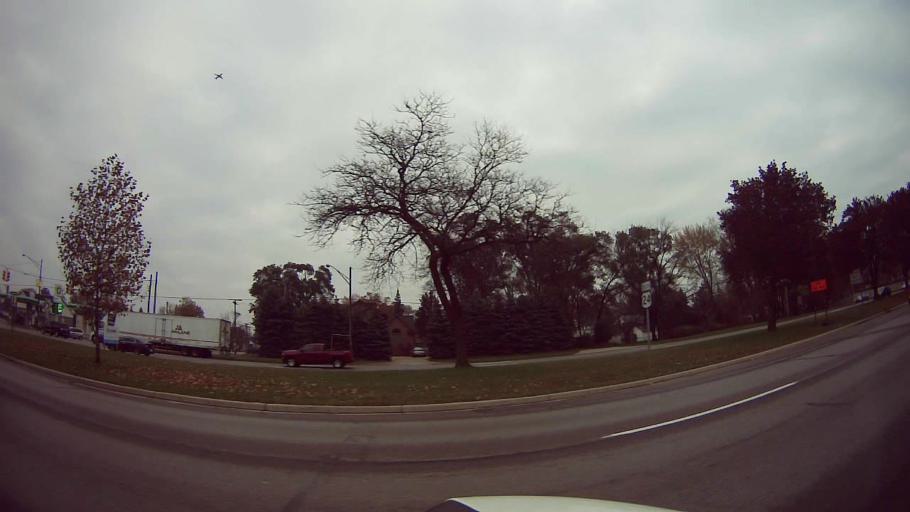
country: US
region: Michigan
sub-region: Wayne County
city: Dearborn Heights
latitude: 42.3126
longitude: -83.2722
